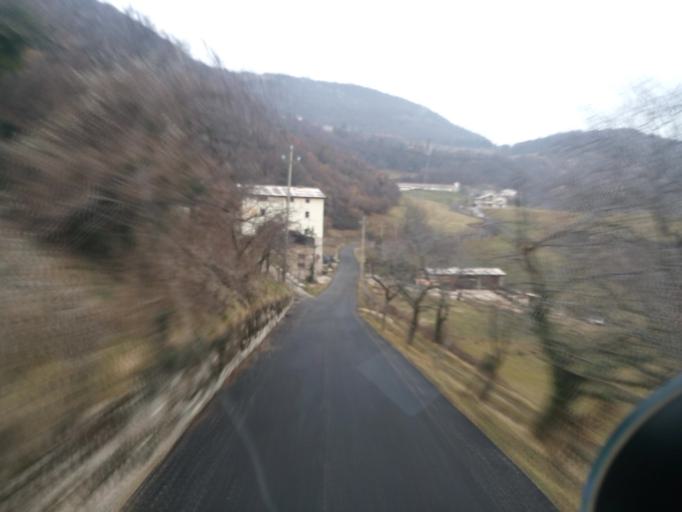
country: IT
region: Veneto
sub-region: Provincia di Verona
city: Dolce
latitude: 45.6047
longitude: 10.8900
